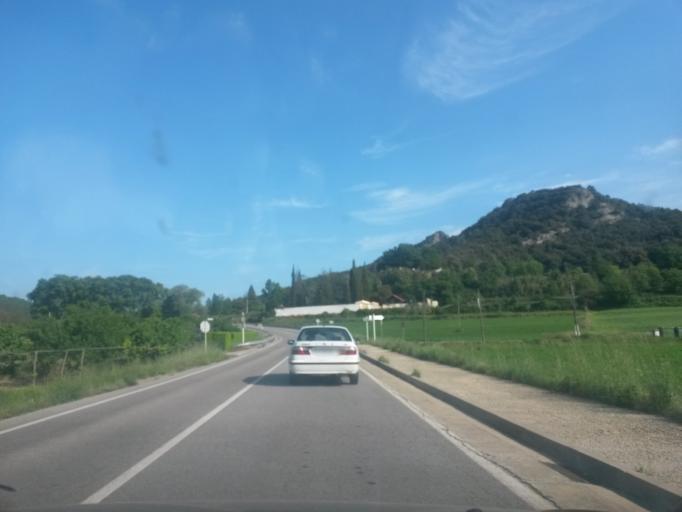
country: ES
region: Catalonia
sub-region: Provincia de Girona
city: les Planes d'Hostoles
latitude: 42.0602
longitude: 2.5361
